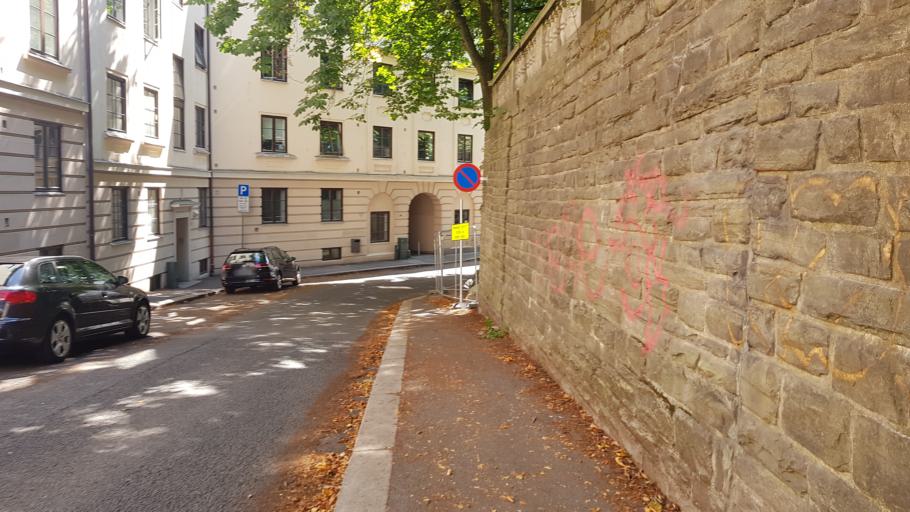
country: NO
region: Oslo
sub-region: Oslo
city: Oslo
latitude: 59.9295
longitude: 10.7479
